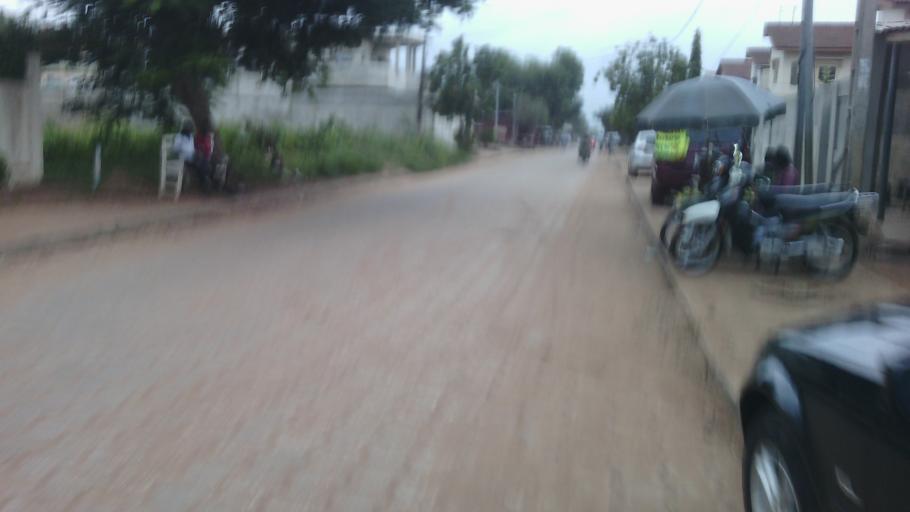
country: BJ
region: Atlantique
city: Abomey-Calavi
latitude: 6.4781
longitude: 2.3518
